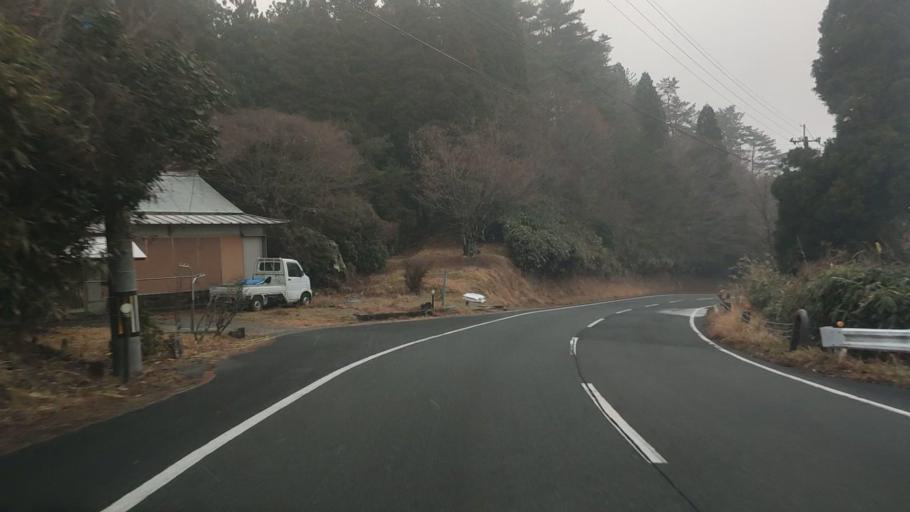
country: JP
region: Kumamoto
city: Matsubase
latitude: 32.5721
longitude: 130.9065
